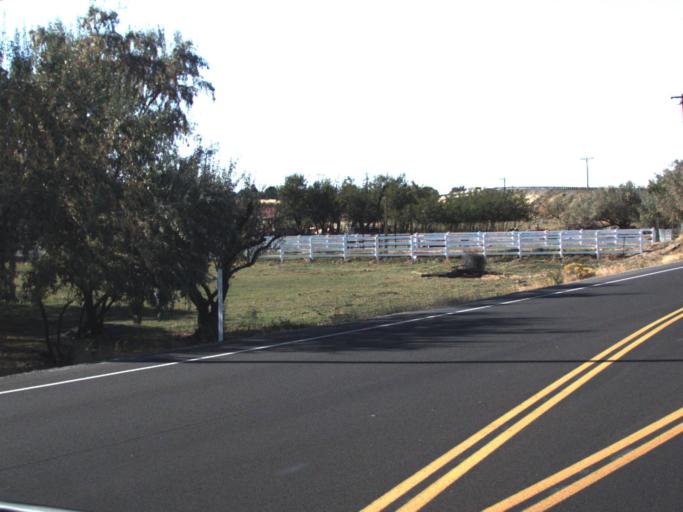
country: US
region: Washington
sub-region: Franklin County
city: Pasco
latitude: 46.1971
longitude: -119.0863
